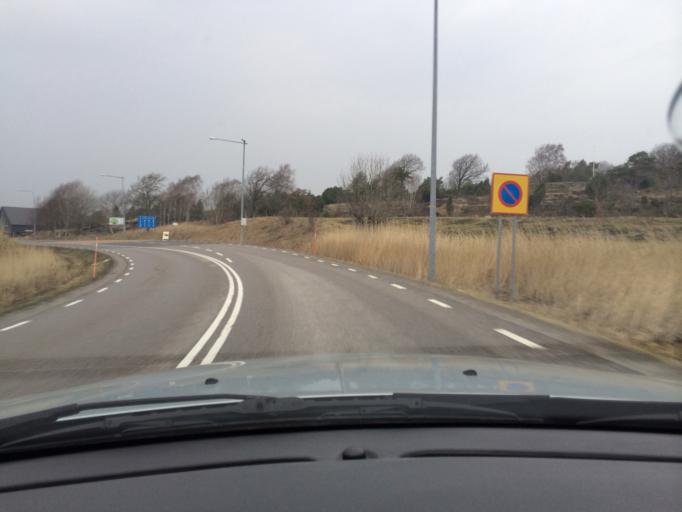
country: SE
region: Vaestra Goetaland
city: Svanesund
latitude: 58.1337
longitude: 11.8482
